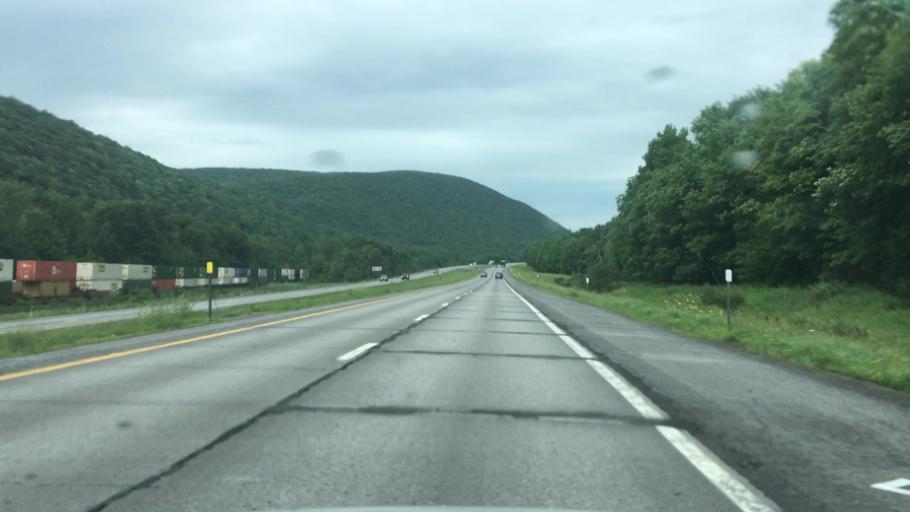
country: US
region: New York
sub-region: Otsego County
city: Worcester
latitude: 42.6367
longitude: -74.6542
